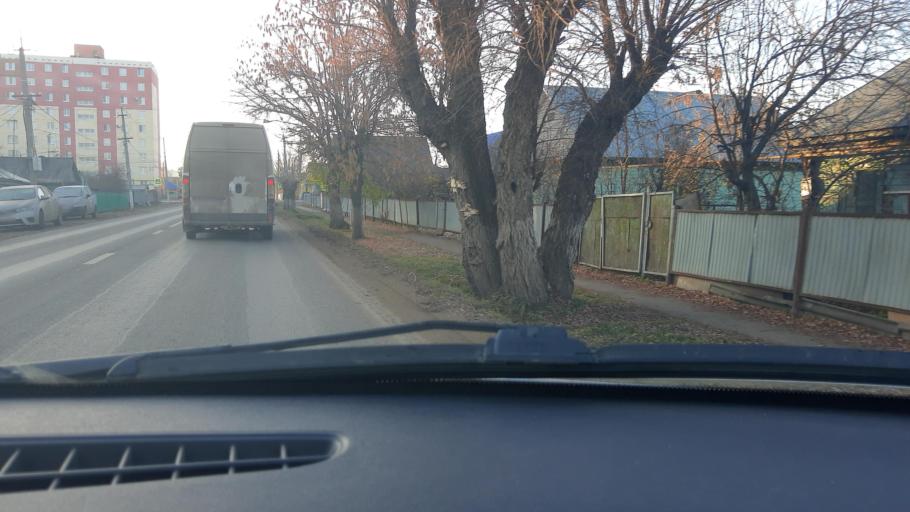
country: RU
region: Bashkortostan
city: Avdon
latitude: 54.7093
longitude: 55.8190
